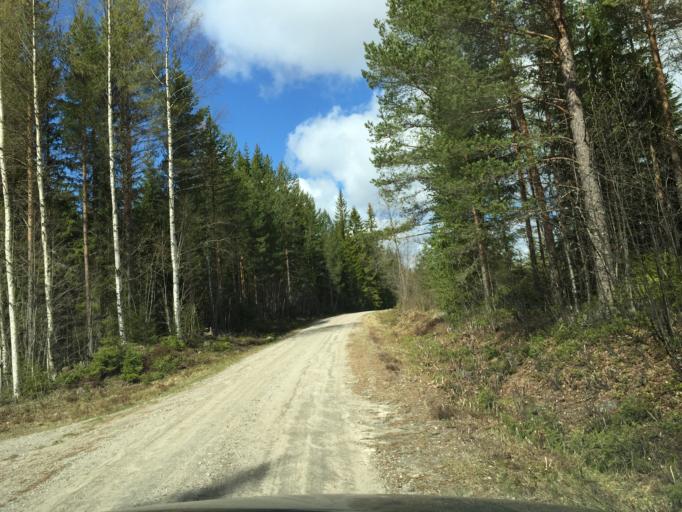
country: SE
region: Gaevleborg
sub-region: Bollnas Kommun
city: Arbra
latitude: 61.5251
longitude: 16.2755
